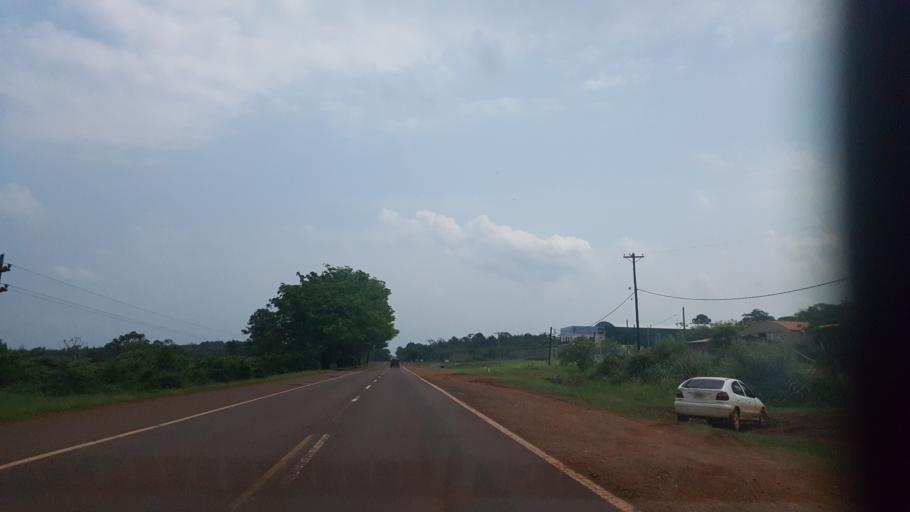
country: AR
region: Misiones
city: Jardin America
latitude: -27.0611
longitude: -55.2605
